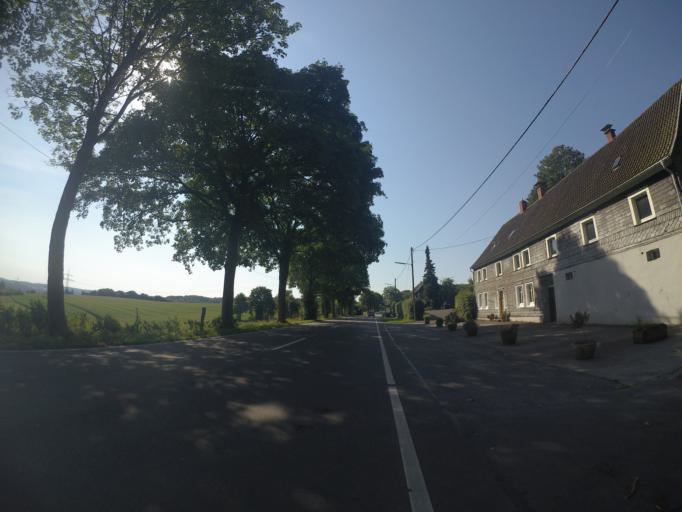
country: DE
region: North Rhine-Westphalia
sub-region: Regierungsbezirk Arnsberg
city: Schwelm
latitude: 51.2398
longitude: 7.2816
